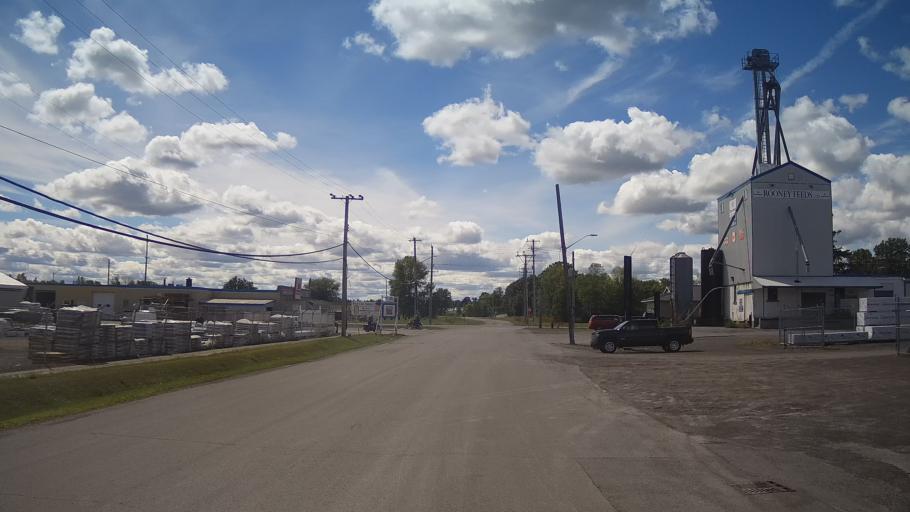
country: US
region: New York
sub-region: St. Lawrence County
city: Ogdensburg
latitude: 44.8460
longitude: -75.3201
